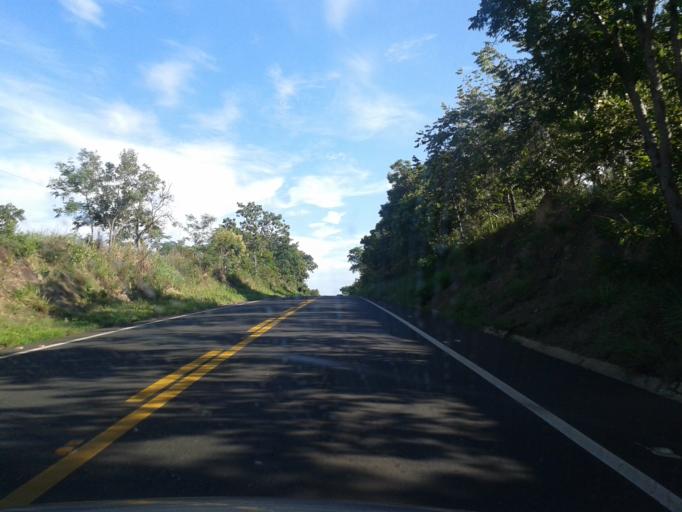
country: BR
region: Goias
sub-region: Caldas Novas
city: Caldas Novas
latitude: -18.1037
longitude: -48.6155
